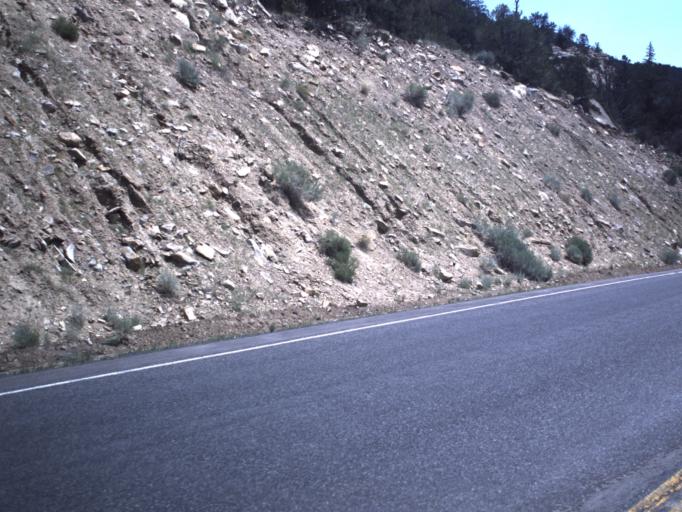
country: US
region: Utah
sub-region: Emery County
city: Huntington
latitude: 39.4172
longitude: -111.1230
